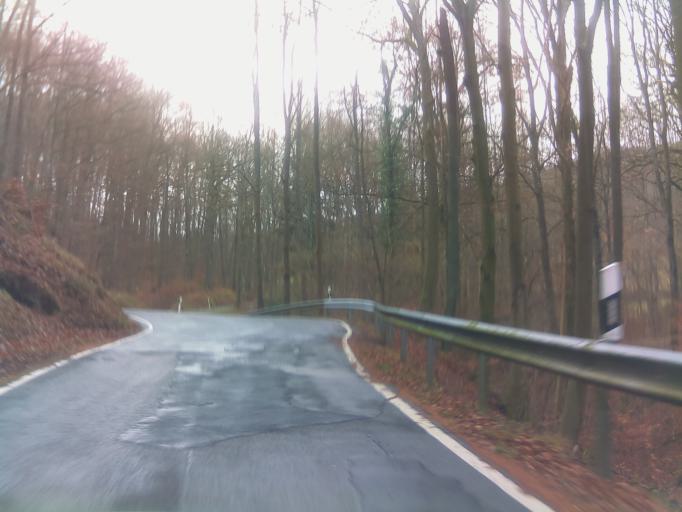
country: DE
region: Rheinland-Pfalz
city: Rockenhausen
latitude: 49.6184
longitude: 7.8466
